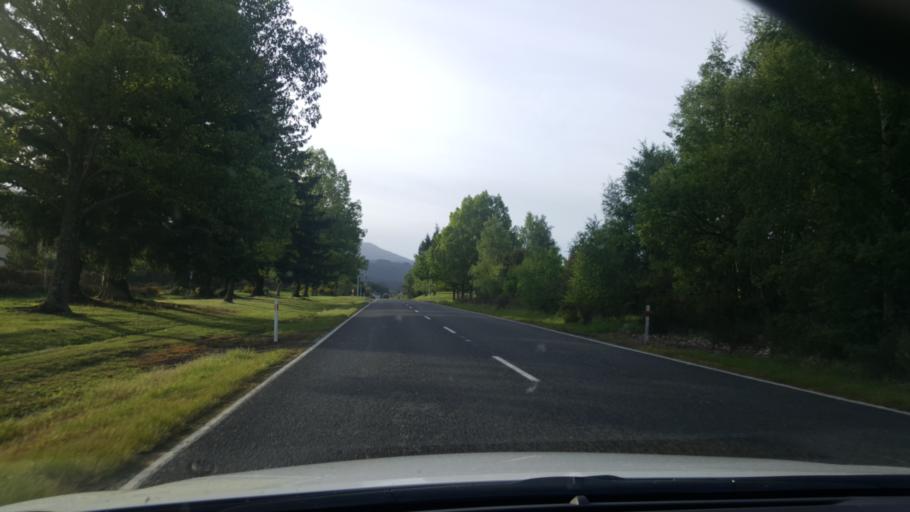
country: NZ
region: Waikato
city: Turangi
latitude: -38.9916
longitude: 175.7954
